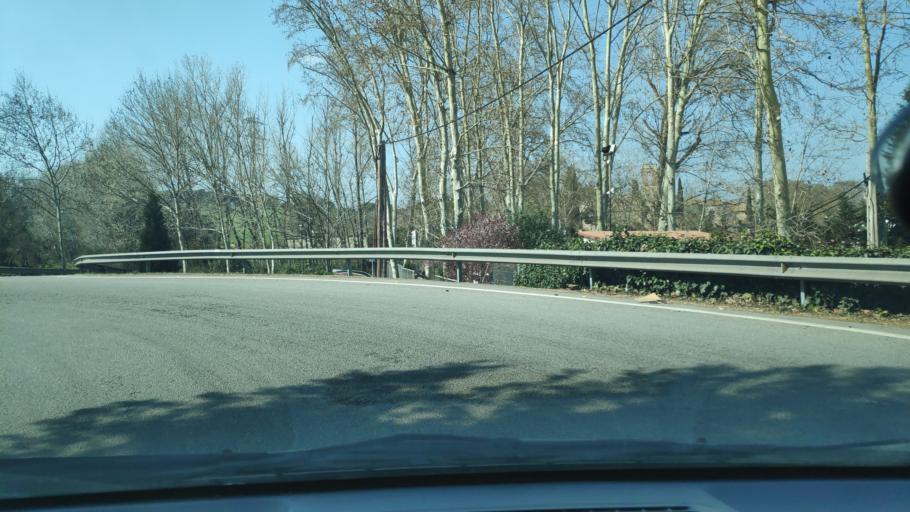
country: ES
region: Catalonia
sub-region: Provincia de Barcelona
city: Polinya
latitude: 41.5333
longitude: 2.1536
